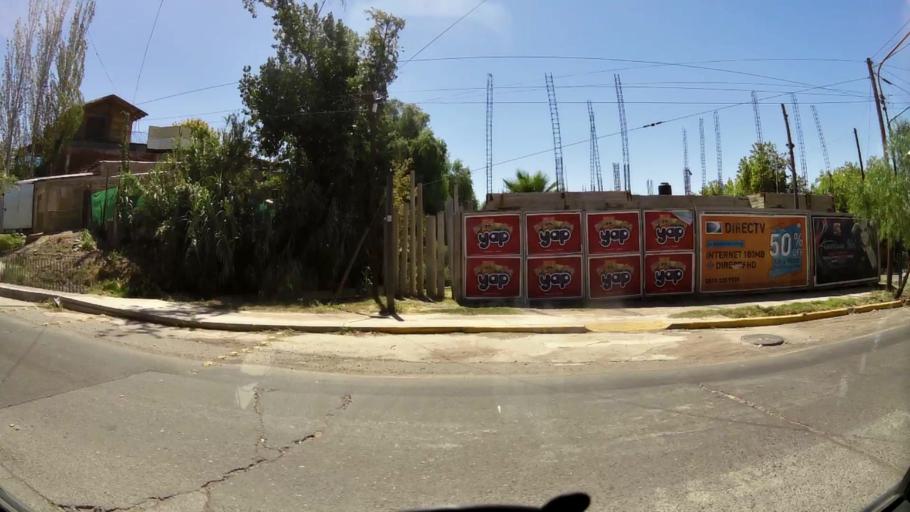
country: AR
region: Mendoza
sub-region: Departamento de Godoy Cruz
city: Godoy Cruz
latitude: -32.9463
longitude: -68.8638
